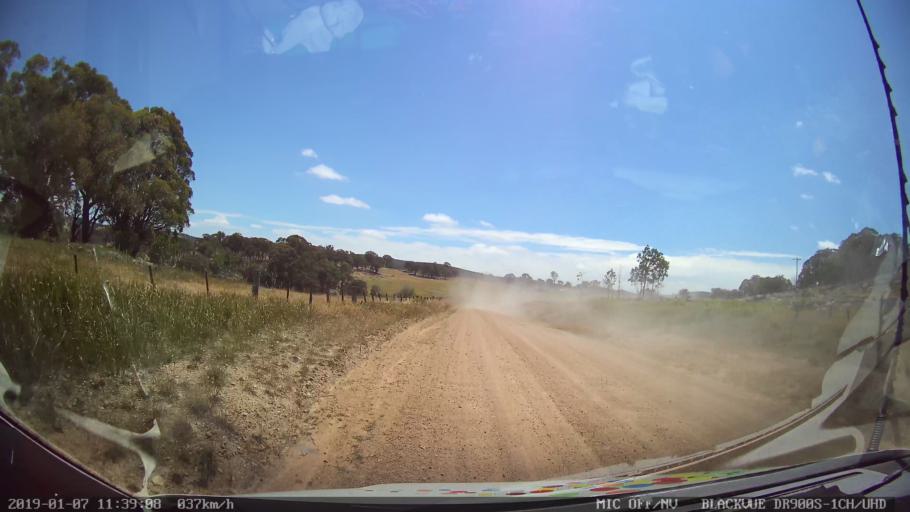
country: AU
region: New South Wales
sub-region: Armidale Dumaresq
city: Armidale
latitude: -30.3686
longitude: 151.5747
